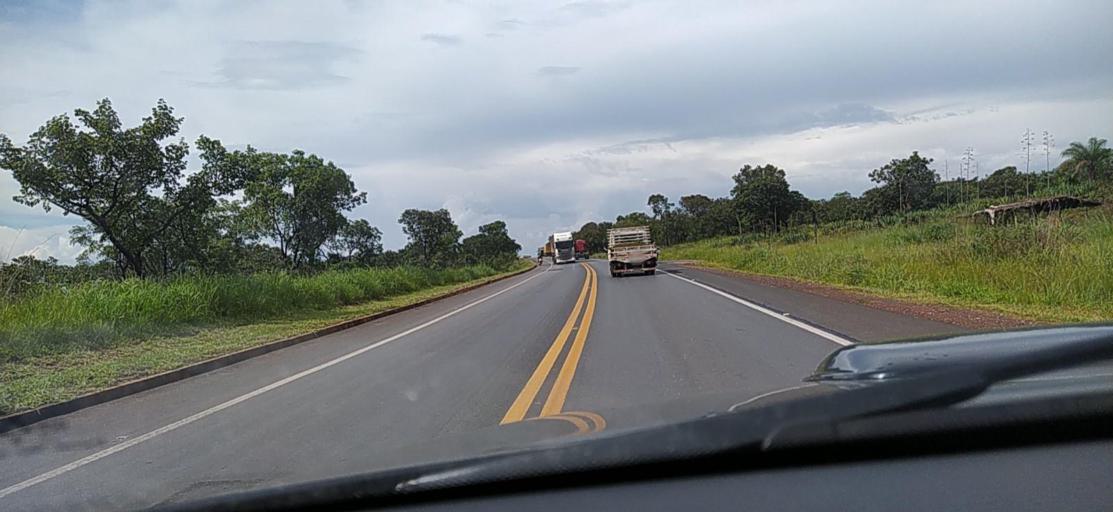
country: BR
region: Minas Gerais
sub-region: Montes Claros
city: Montes Claros
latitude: -16.8680
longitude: -43.8543
